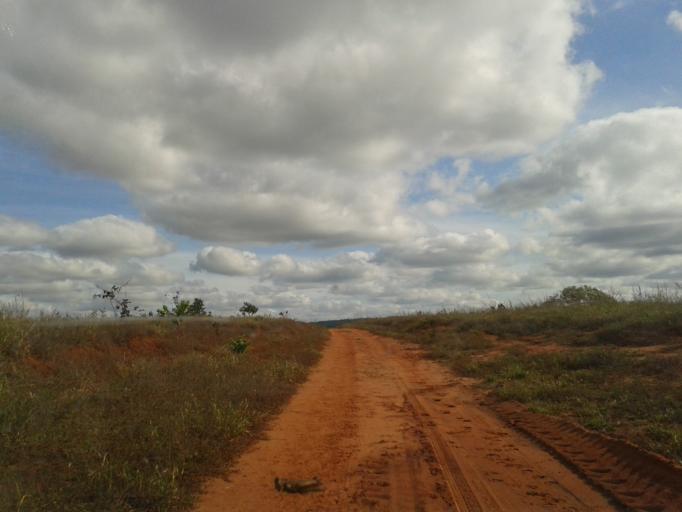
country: BR
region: Minas Gerais
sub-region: Campina Verde
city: Campina Verde
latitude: -19.4364
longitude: -49.7253
